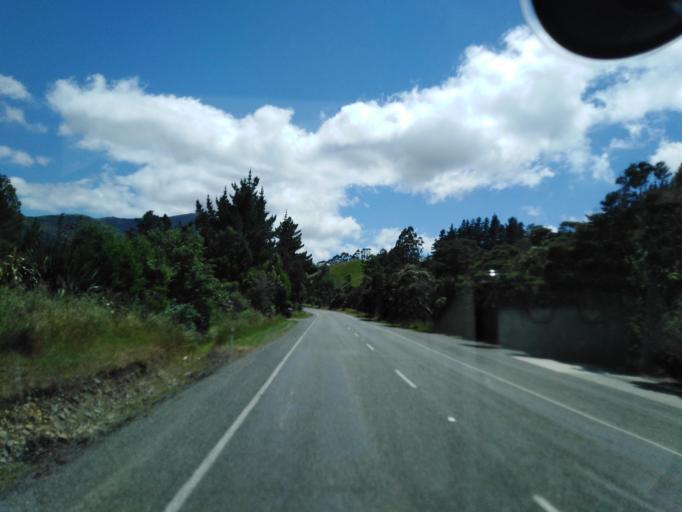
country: NZ
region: Nelson
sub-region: Nelson City
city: Nelson
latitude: -41.2220
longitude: 173.3973
